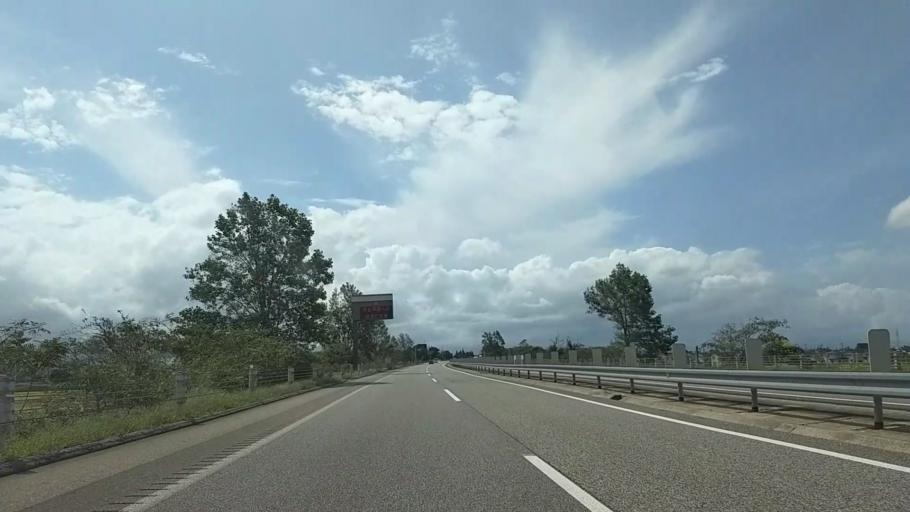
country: JP
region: Toyama
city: Kamiichi
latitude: 36.6903
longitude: 137.3290
